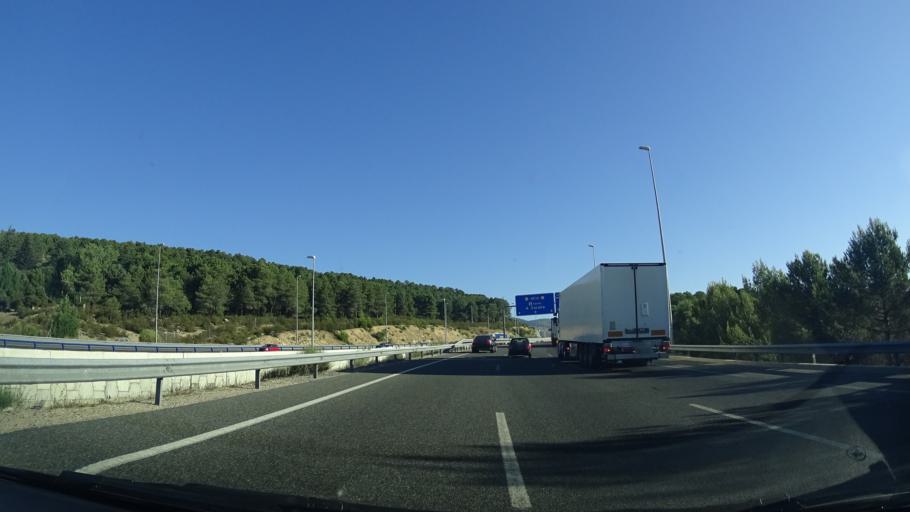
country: ES
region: Madrid
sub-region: Provincia de Madrid
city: Guadarrama
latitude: 40.6801
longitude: -4.1178
